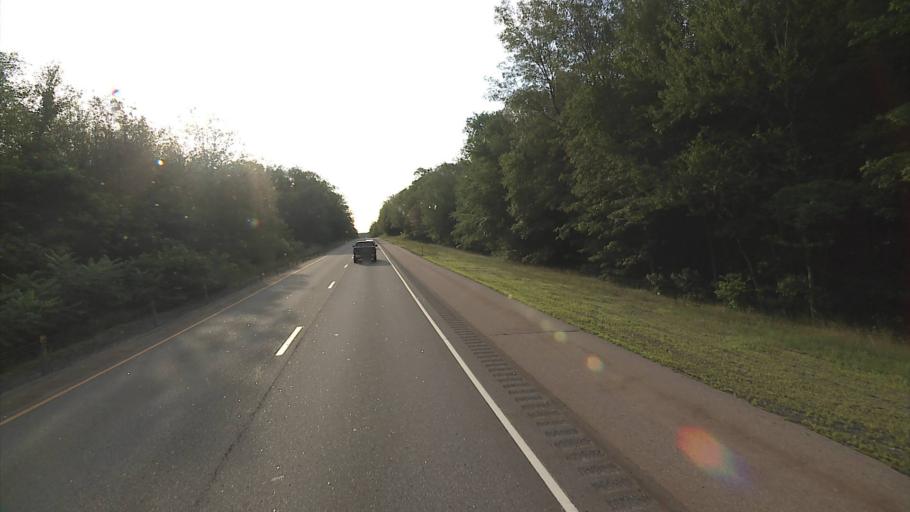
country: US
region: Connecticut
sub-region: New London County
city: Colchester
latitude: 41.5678
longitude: -72.2684
